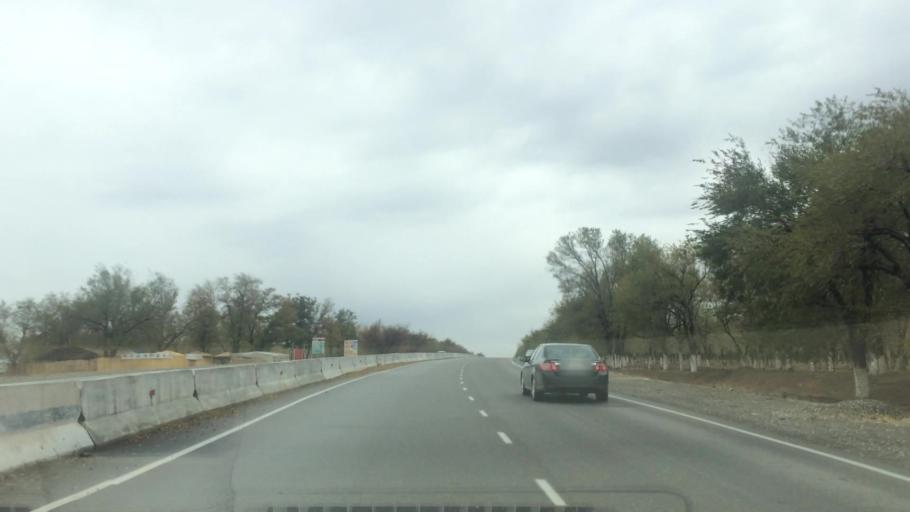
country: UZ
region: Samarqand
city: Bulung'ur
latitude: 39.9186
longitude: 67.5151
